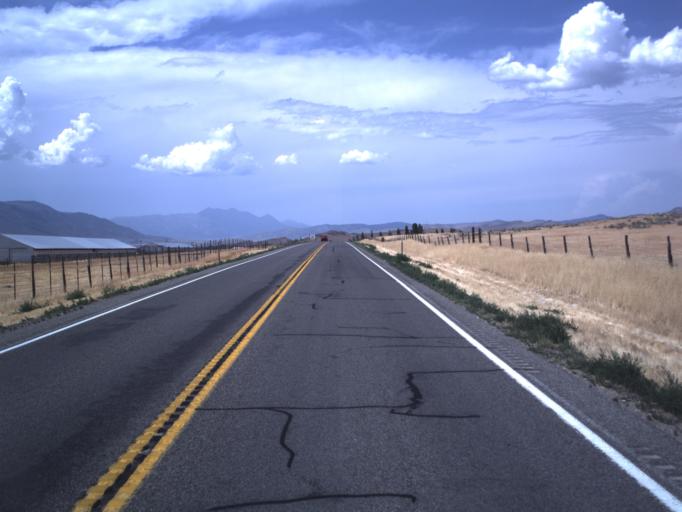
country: US
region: Utah
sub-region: Sanpete County
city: Moroni
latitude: 39.4965
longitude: -111.5641
